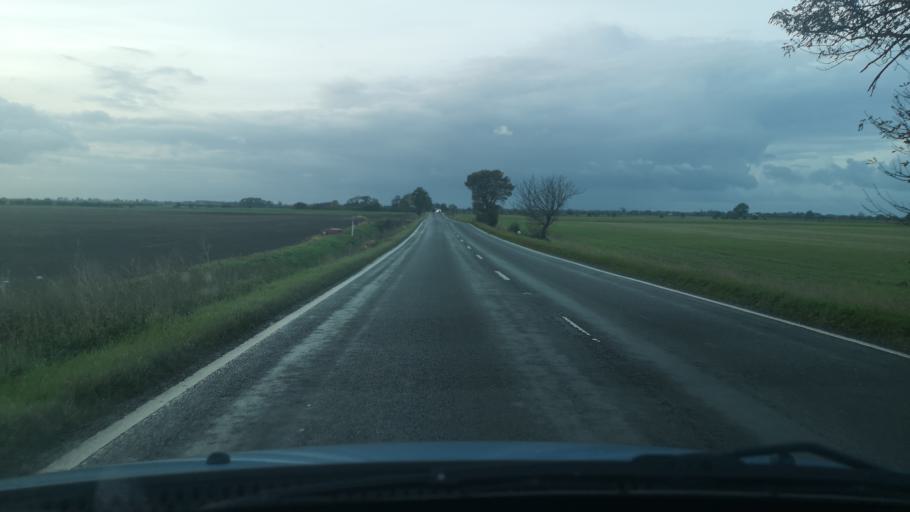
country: GB
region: England
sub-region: Doncaster
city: Hatfield
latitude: 53.5884
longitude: -0.9223
